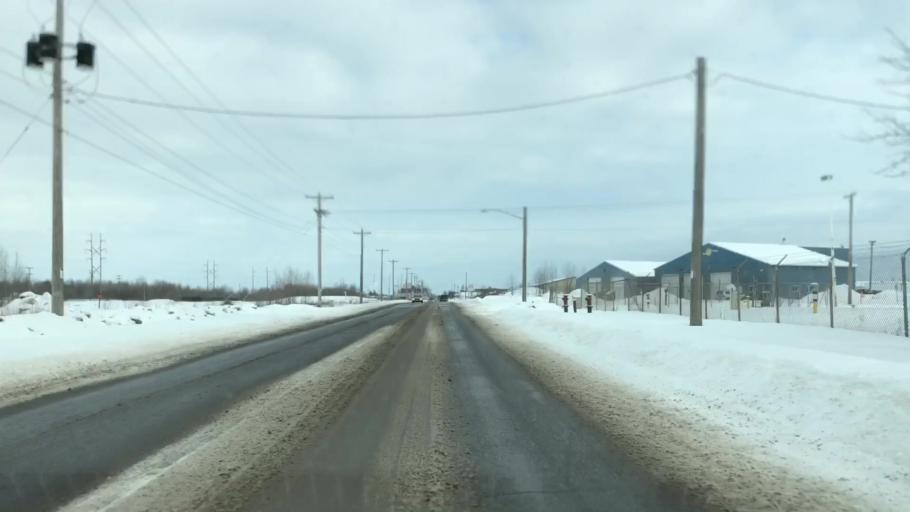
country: US
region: Wisconsin
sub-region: Douglas County
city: Superior
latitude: 46.7280
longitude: -92.1216
